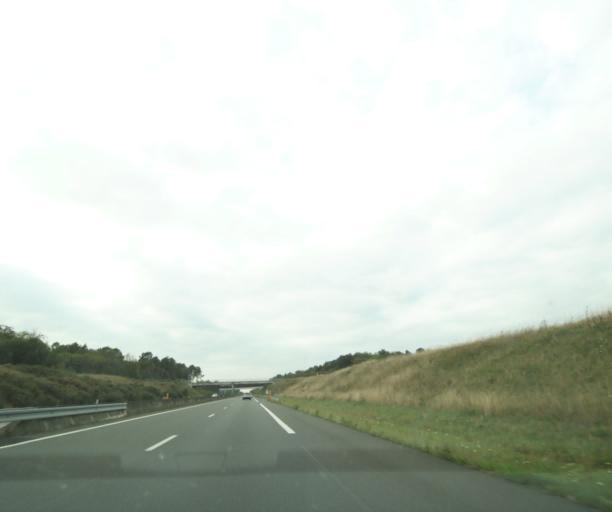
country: FR
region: Pays de la Loire
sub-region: Departement de la Sarthe
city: Luceau
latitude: 47.6936
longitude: 0.3604
